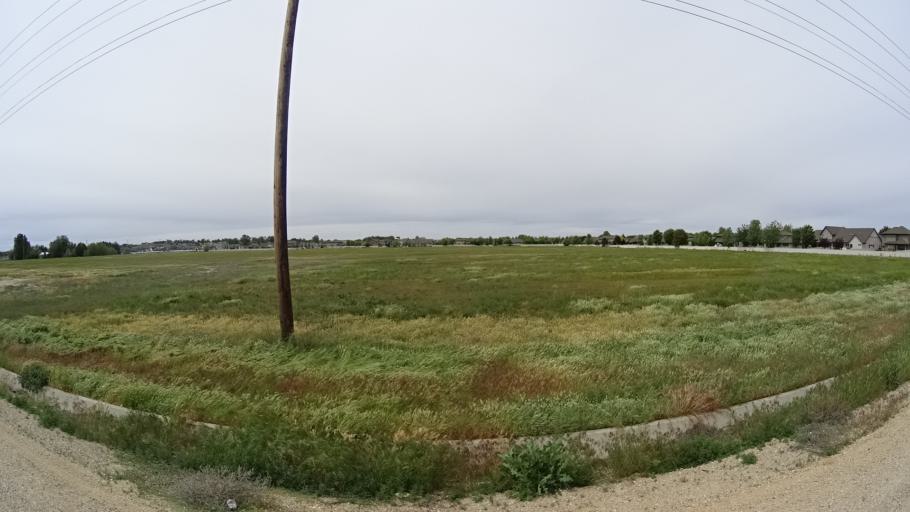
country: US
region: Idaho
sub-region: Ada County
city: Meridian
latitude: 43.5638
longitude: -116.3541
